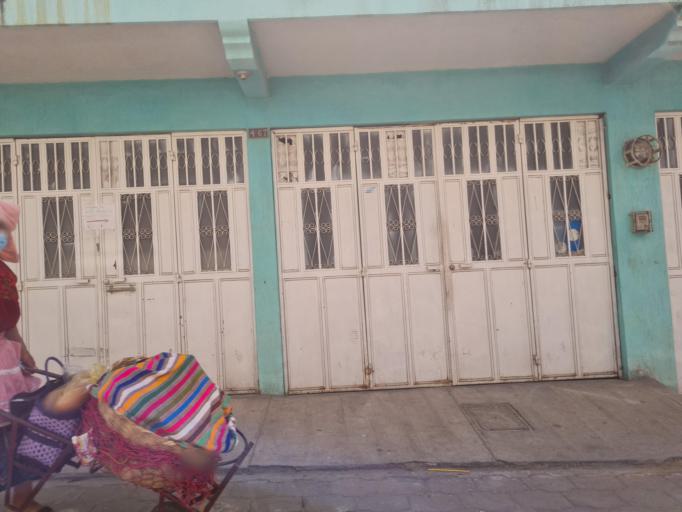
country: GT
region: Quetzaltenango
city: Quetzaltenango
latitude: 14.8378
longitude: -91.5330
